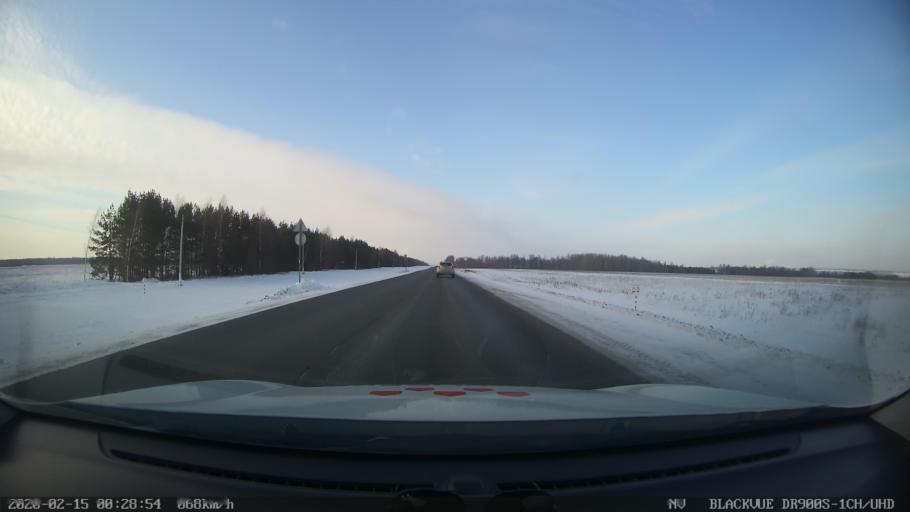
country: RU
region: Tatarstan
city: Verkhniy Uslon
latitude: 55.6464
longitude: 48.8736
